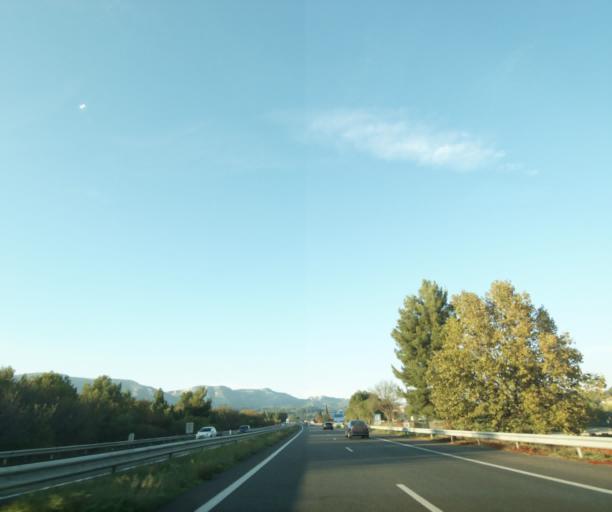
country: FR
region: Provence-Alpes-Cote d'Azur
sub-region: Departement des Bouches-du-Rhone
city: Aubagne
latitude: 43.3115
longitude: 5.5917
